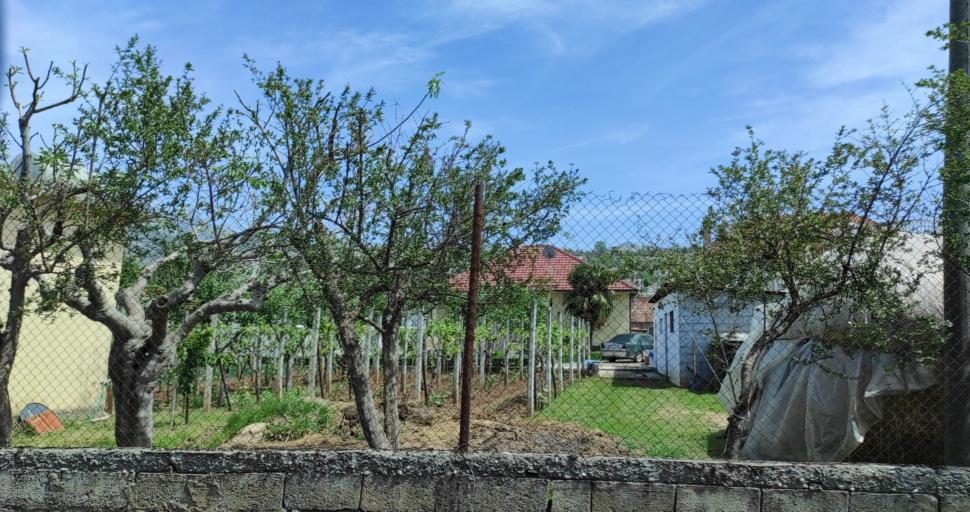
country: AL
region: Shkoder
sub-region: Rrethi i Malesia e Madhe
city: Gruemire
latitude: 42.1280
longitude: 19.5546
